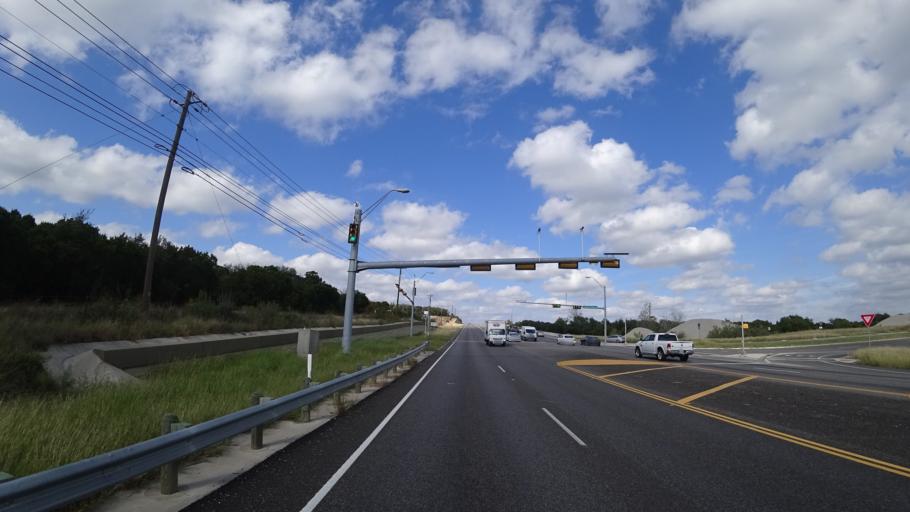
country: US
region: Texas
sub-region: Travis County
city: Bee Cave
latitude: 30.2750
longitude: -97.9141
